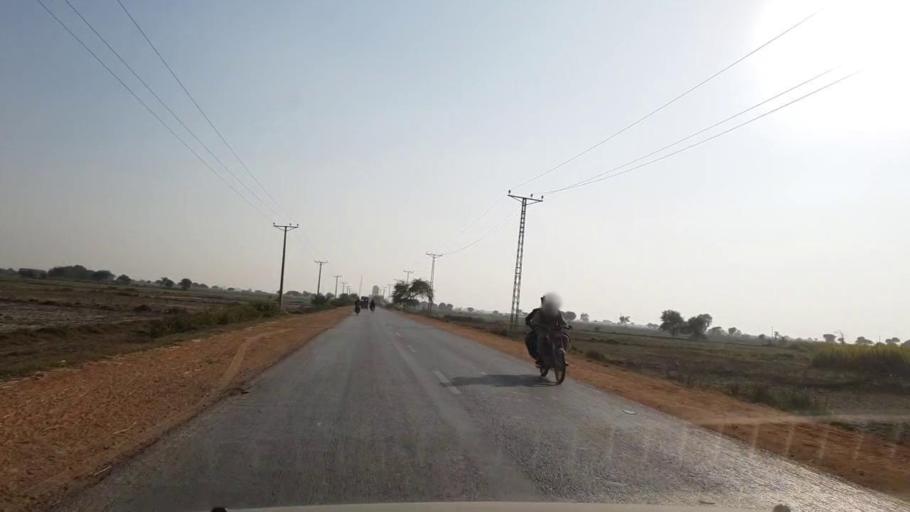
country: PK
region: Sindh
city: Bulri
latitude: 24.8420
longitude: 68.3252
